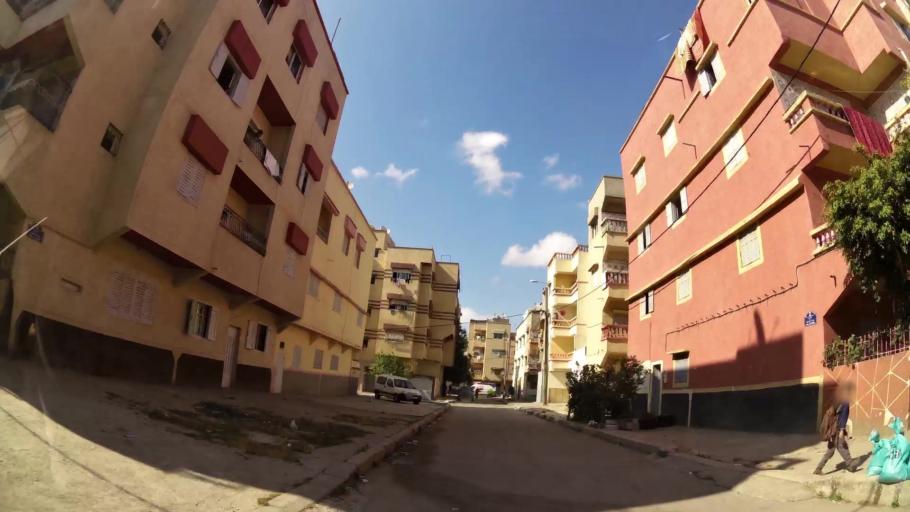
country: MA
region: Rabat-Sale-Zemmour-Zaer
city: Sale
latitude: 34.0425
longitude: -6.7785
